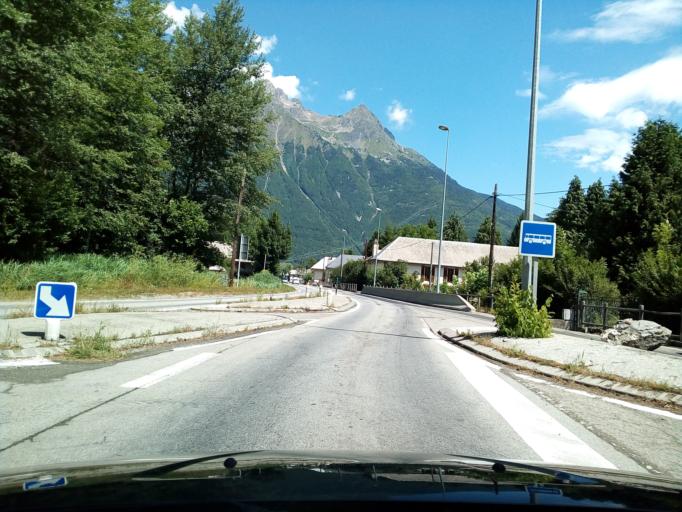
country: FR
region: Rhone-Alpes
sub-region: Departement de l'Isere
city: Huez
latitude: 45.0977
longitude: 6.0096
